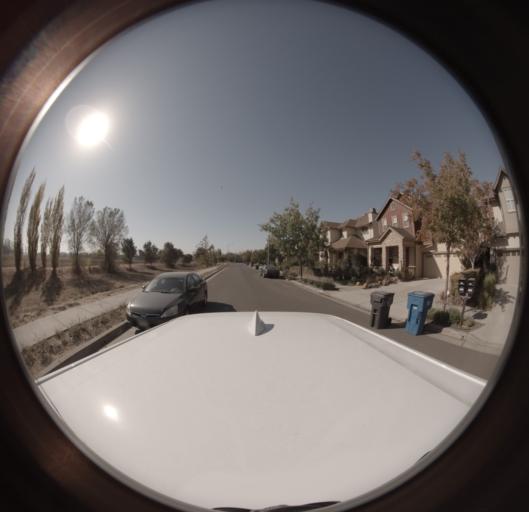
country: US
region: California
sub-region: Sonoma County
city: Petaluma
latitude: 38.2377
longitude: -122.5871
